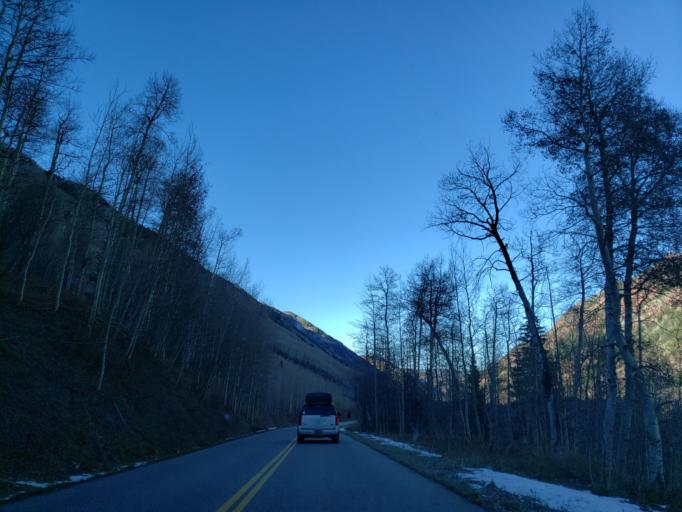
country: US
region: Colorado
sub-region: Pitkin County
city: Snowmass Village
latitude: 39.1156
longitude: -106.9113
